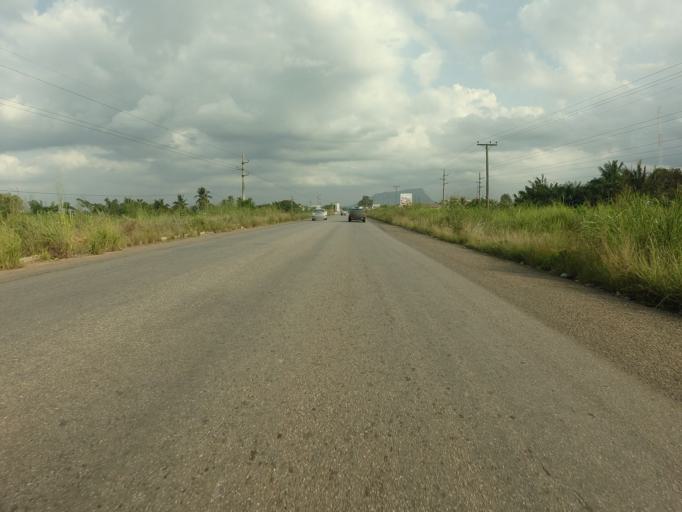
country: GH
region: Volta
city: Ho
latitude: 6.5862
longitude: 0.4796
